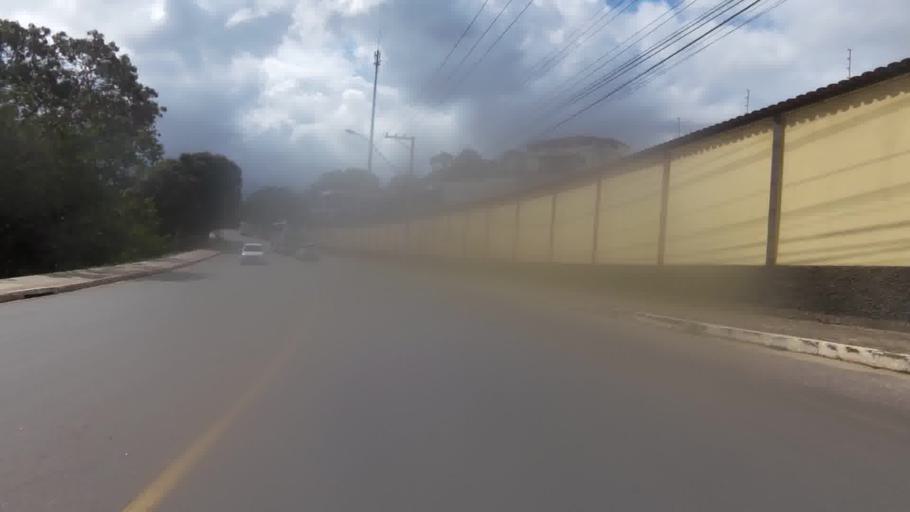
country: BR
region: Espirito Santo
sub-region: Piuma
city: Piuma
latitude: -20.8082
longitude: -40.6583
